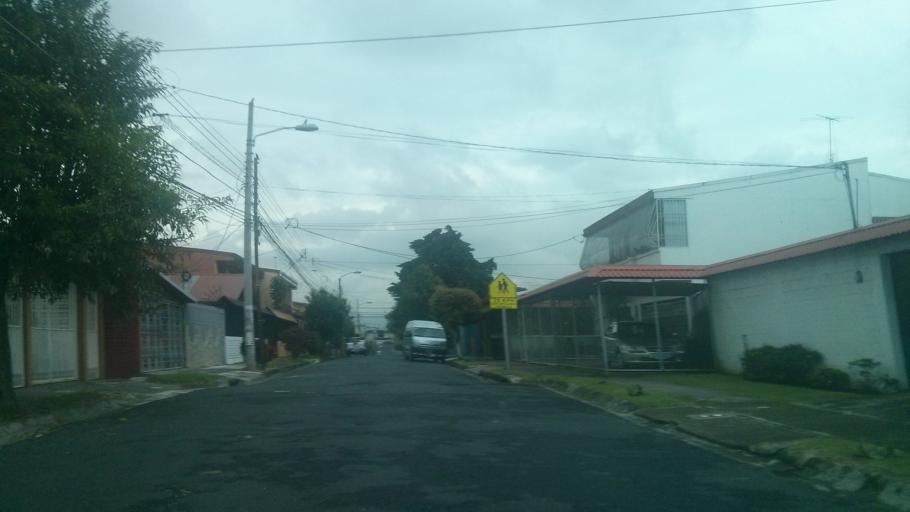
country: CR
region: San Jose
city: San Pedro
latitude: 9.9079
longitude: -84.0584
